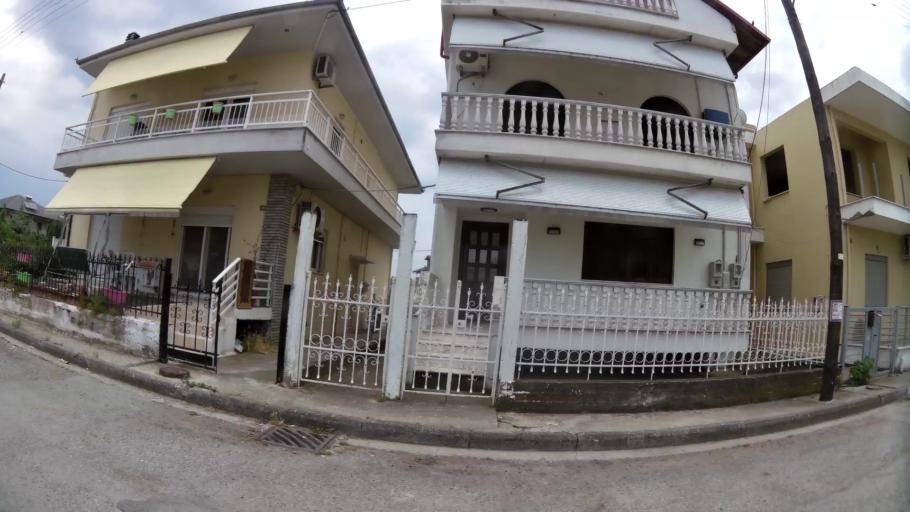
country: GR
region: Central Macedonia
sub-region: Nomos Pierias
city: Kallithea
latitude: 40.2724
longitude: 22.5763
